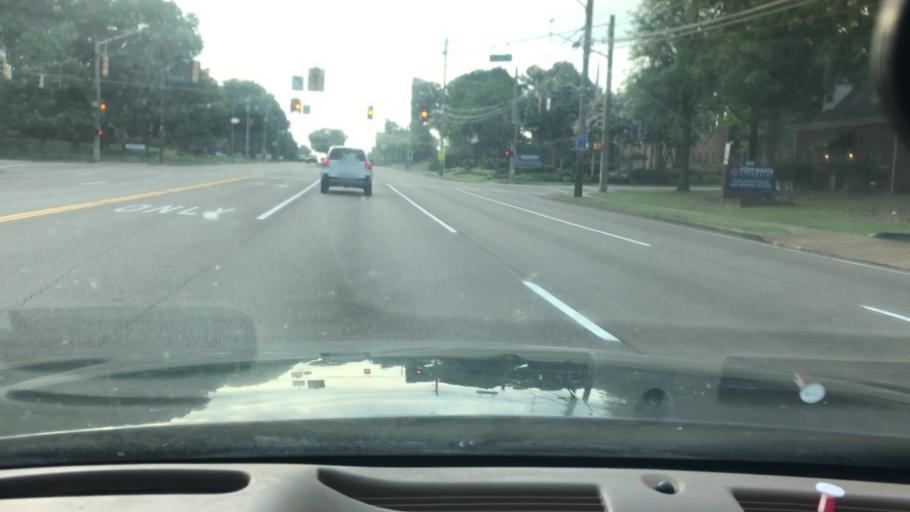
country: US
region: Tennessee
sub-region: Shelby County
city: Bartlett
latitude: 35.2047
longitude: -89.8488
